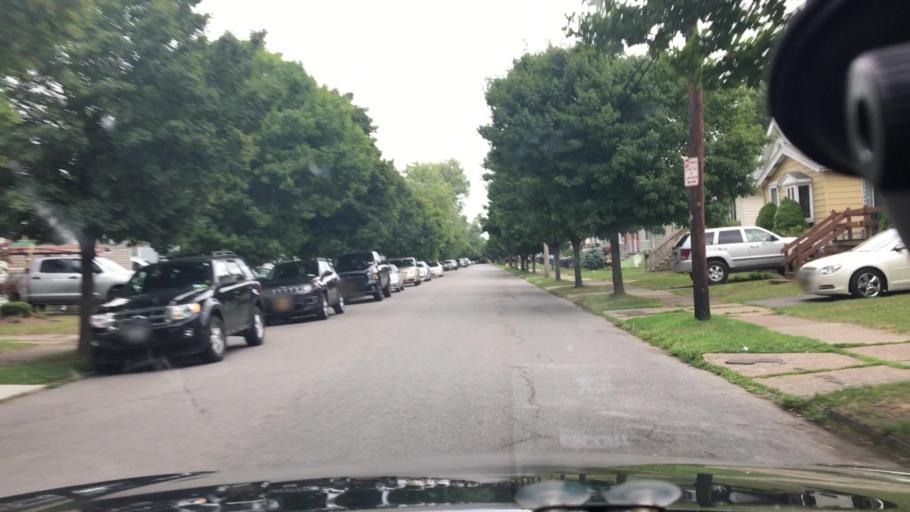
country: US
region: New York
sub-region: Erie County
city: Lackawanna
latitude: 42.8372
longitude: -78.8203
